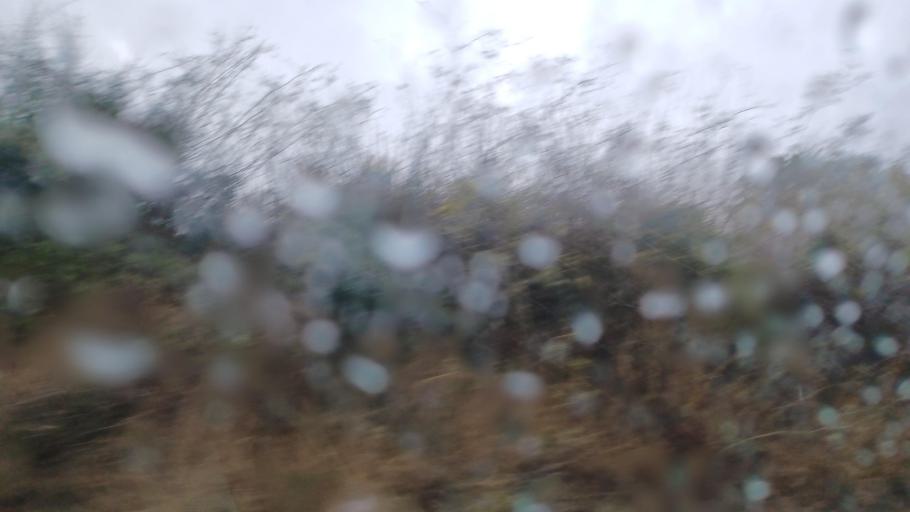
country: CY
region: Pafos
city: Tala
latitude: 34.8907
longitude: 32.4704
